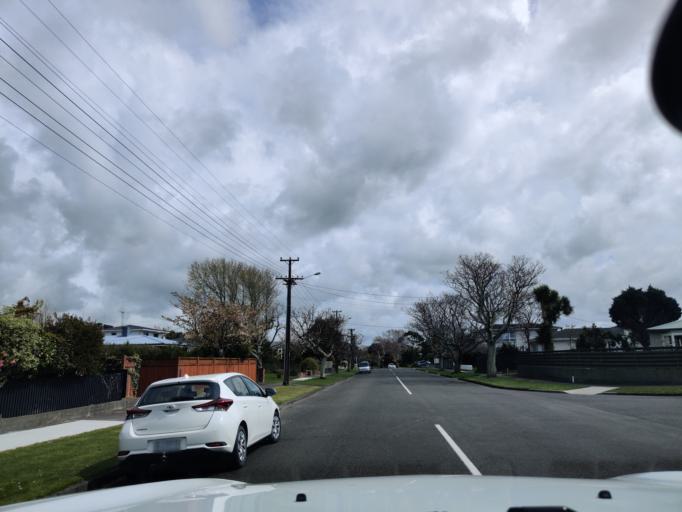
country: NZ
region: Manawatu-Wanganui
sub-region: Palmerston North City
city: Palmerston North
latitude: -40.3800
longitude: 175.5902
